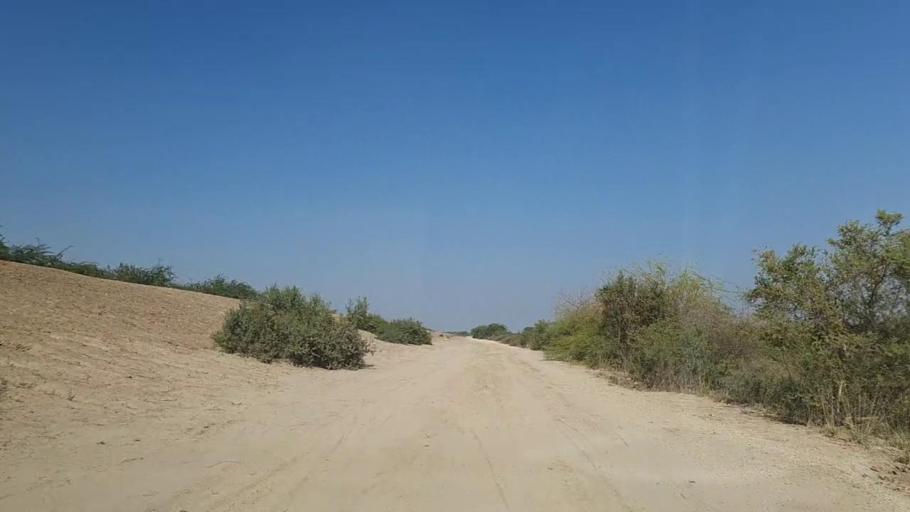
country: PK
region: Sindh
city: Chuhar Jamali
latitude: 24.4781
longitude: 68.0113
